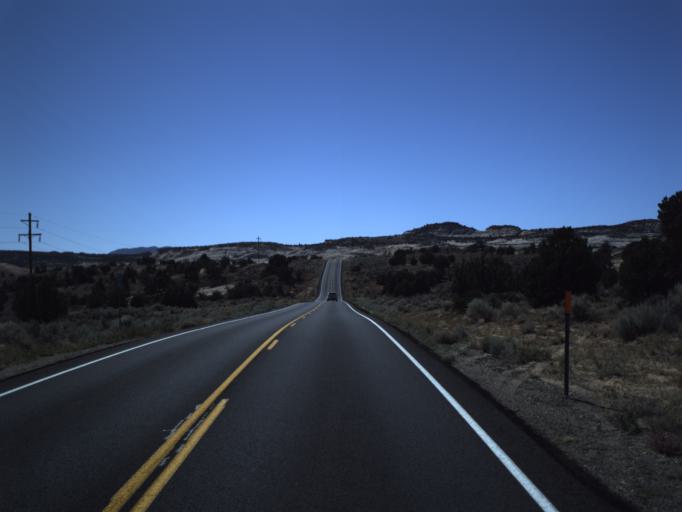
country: US
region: Utah
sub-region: Wayne County
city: Loa
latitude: 37.7600
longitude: -111.4321
